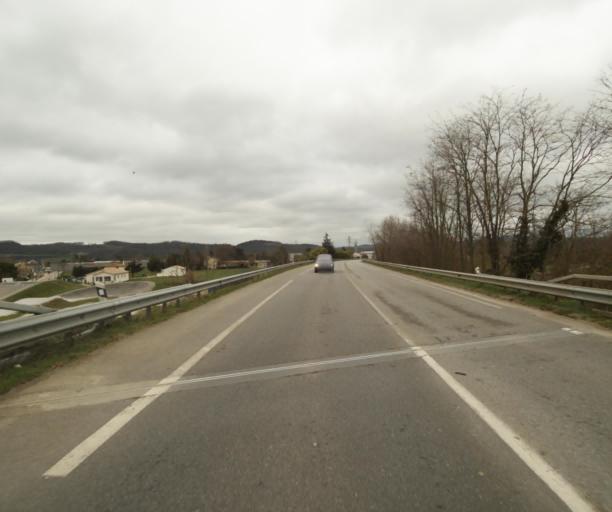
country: FR
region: Midi-Pyrenees
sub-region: Departement de l'Ariege
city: Pamiers
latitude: 43.1380
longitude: 1.6125
